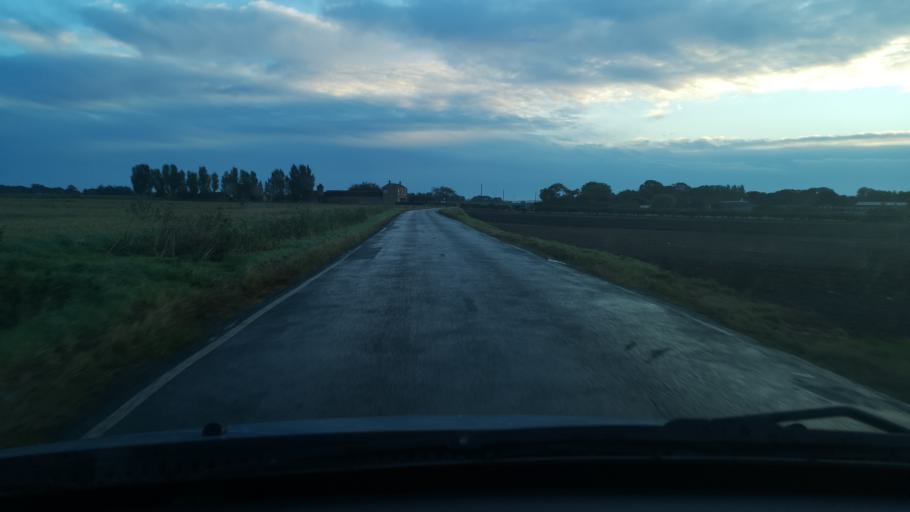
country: GB
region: England
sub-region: East Riding of Yorkshire
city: Laxton
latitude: 53.6981
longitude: -0.8113
